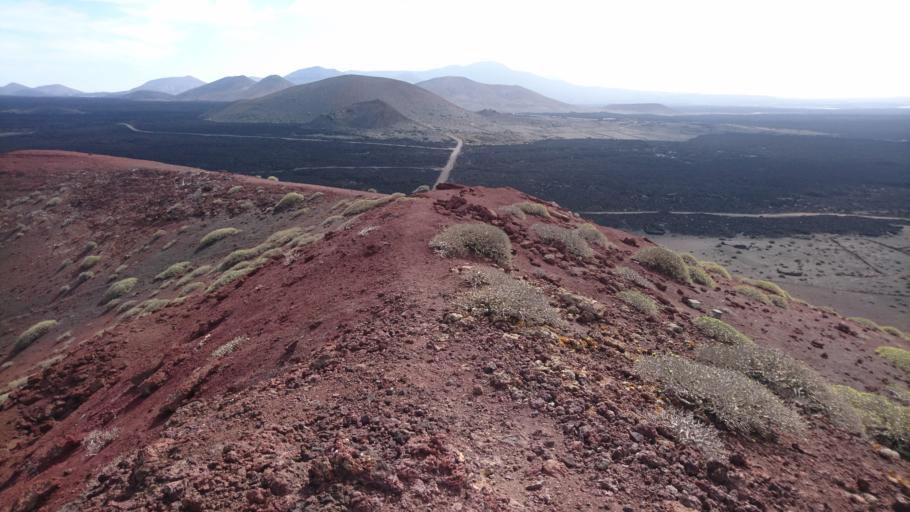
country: ES
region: Canary Islands
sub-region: Provincia de Las Palmas
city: Yaiza
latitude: 28.9883
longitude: -13.8159
